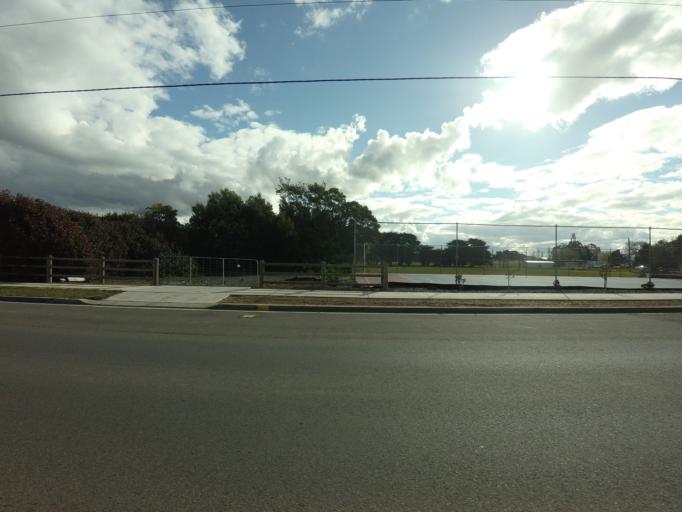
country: AU
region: Tasmania
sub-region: Northern Midlands
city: Longford
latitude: -41.6922
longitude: 147.0790
